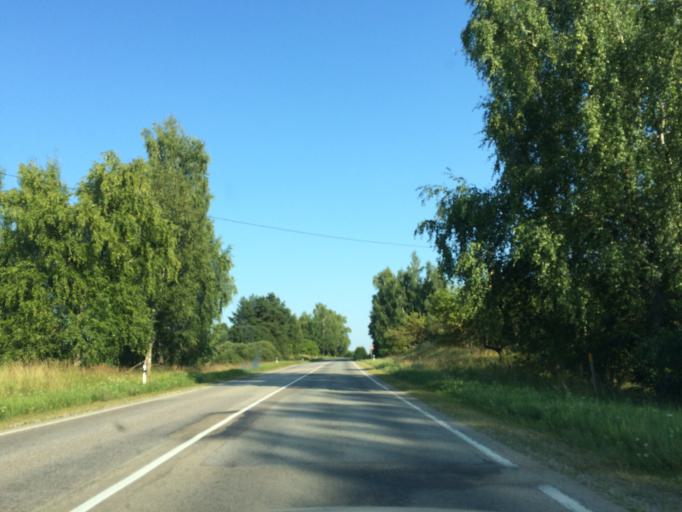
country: LV
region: Ludzas Rajons
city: Ludza
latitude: 56.5382
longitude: 27.5750
